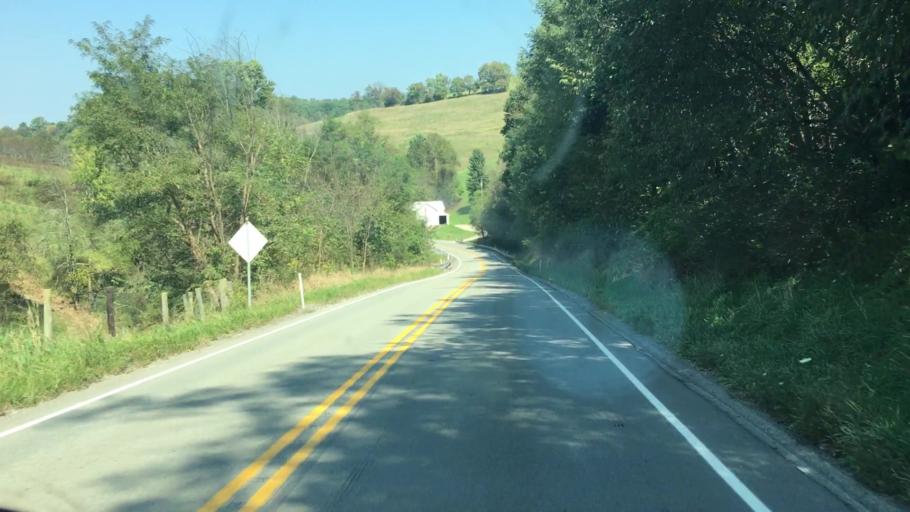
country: US
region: Pennsylvania
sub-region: Greene County
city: Waynesburg
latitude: 39.9866
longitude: -80.3474
